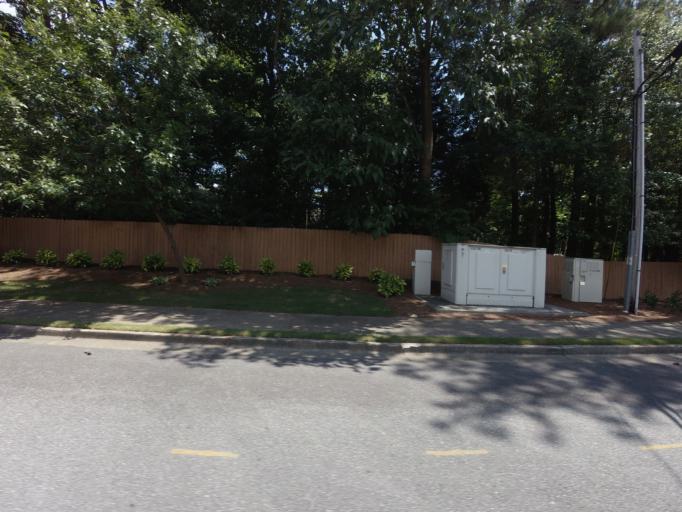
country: US
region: Georgia
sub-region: Fulton County
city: Johns Creek
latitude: 34.0414
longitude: -84.2078
